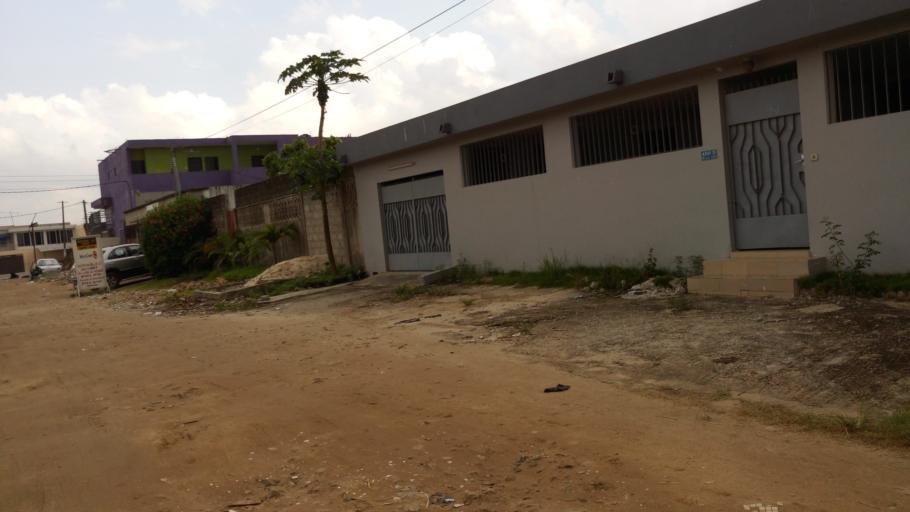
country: CI
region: Lagunes
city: Abobo
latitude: 5.3988
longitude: -4.0057
